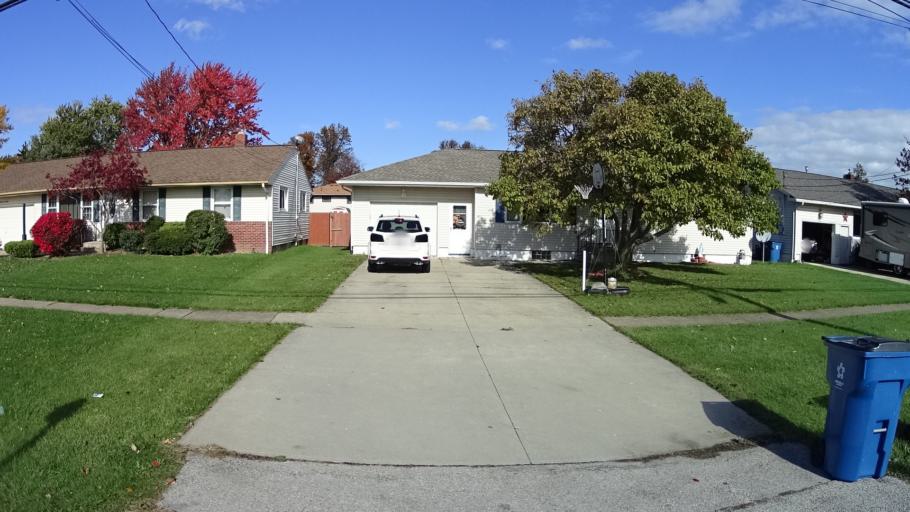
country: US
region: Ohio
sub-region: Lorain County
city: Lorain
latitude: 41.4418
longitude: -82.2179
